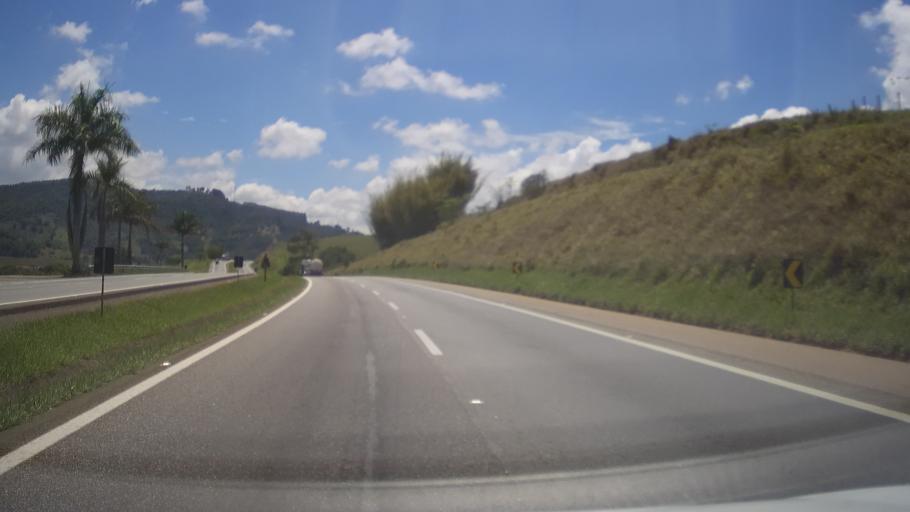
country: BR
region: Minas Gerais
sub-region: Campanha
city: Campanha
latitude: -21.8220
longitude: -45.4940
